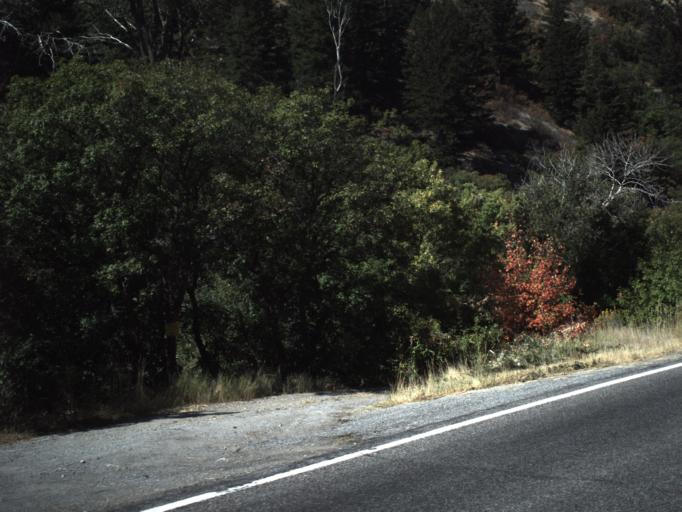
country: US
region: Utah
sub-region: Cache County
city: Hyrum
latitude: 41.6214
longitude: -111.7820
